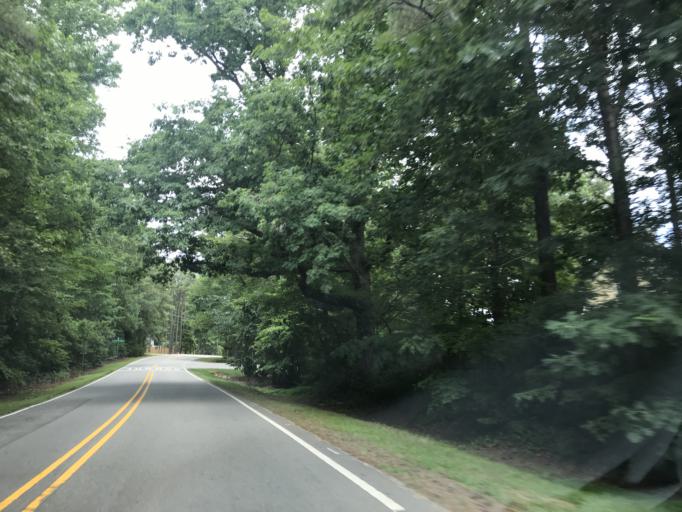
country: US
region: North Carolina
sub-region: Wake County
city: West Raleigh
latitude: 35.9118
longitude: -78.6947
